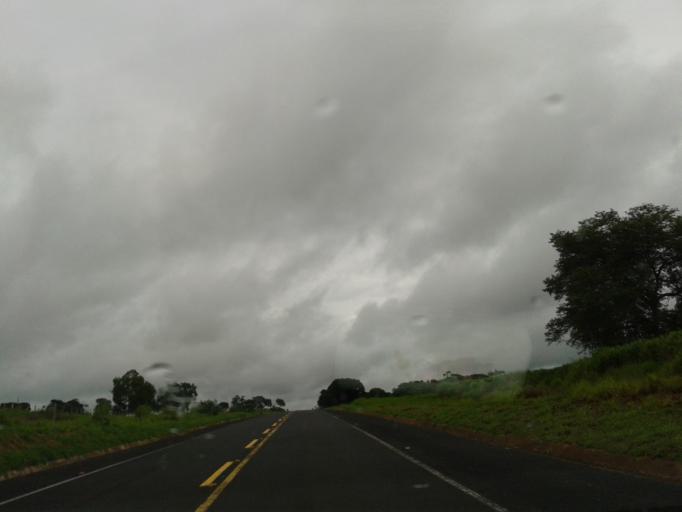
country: BR
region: Minas Gerais
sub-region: Santa Vitoria
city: Santa Vitoria
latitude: -19.2332
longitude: -50.0173
